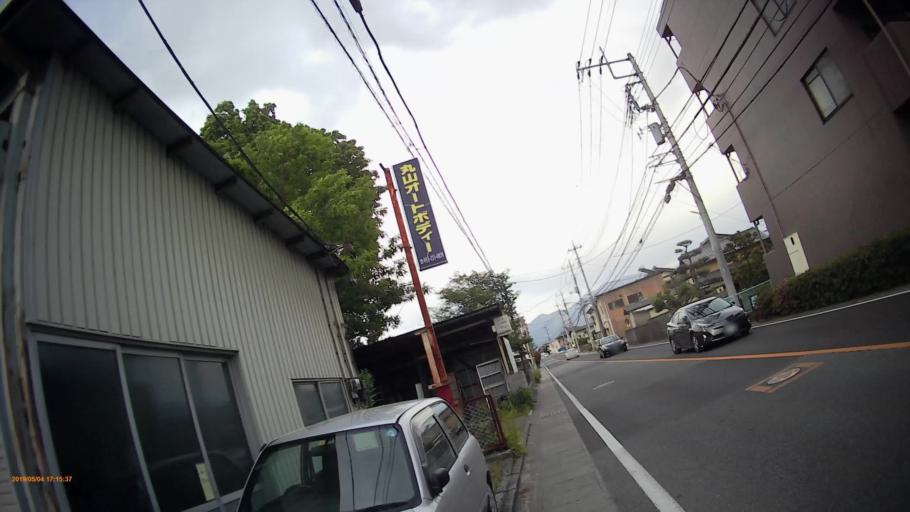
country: JP
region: Yamanashi
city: Isawa
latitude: 35.6519
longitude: 138.6281
